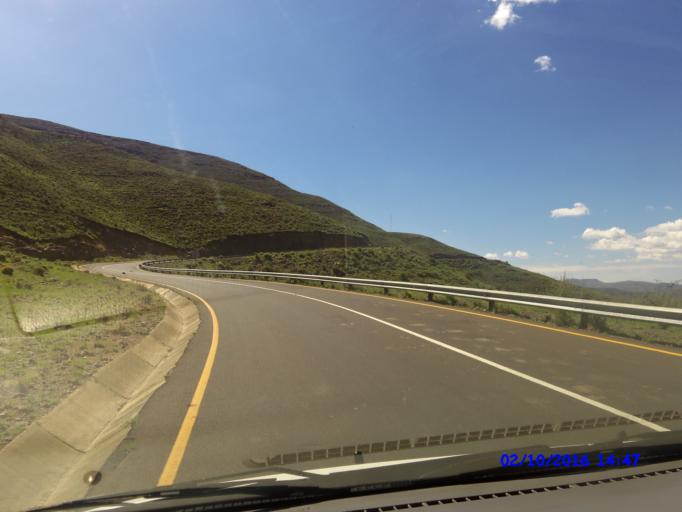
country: LS
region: Maseru
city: Nako
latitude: -29.5034
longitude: 28.0633
